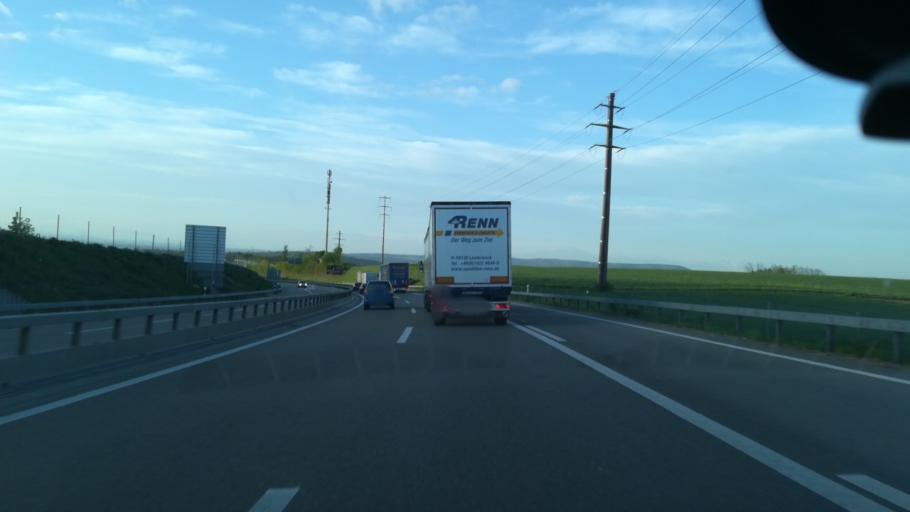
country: CH
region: Zurich
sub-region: Bezirk Andelfingen
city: Dachsen
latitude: 47.6712
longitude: 8.6224
